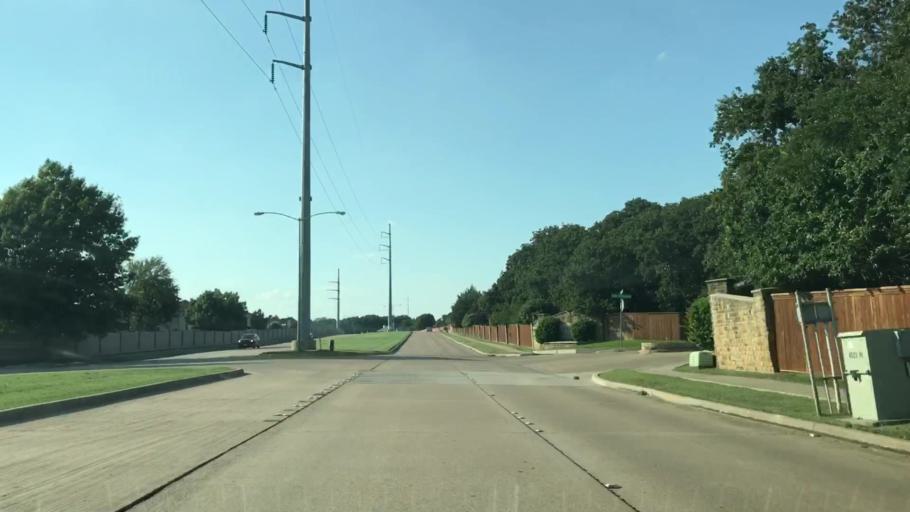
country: US
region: Texas
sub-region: Denton County
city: Lewisville
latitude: 33.0299
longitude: -97.0316
